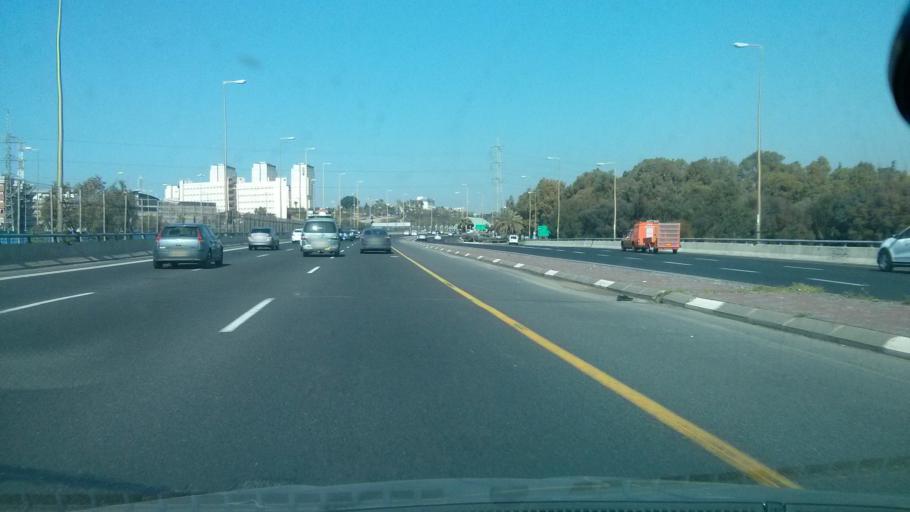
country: IL
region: Tel Aviv
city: Ramat Gan
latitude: 32.0987
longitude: 34.8028
